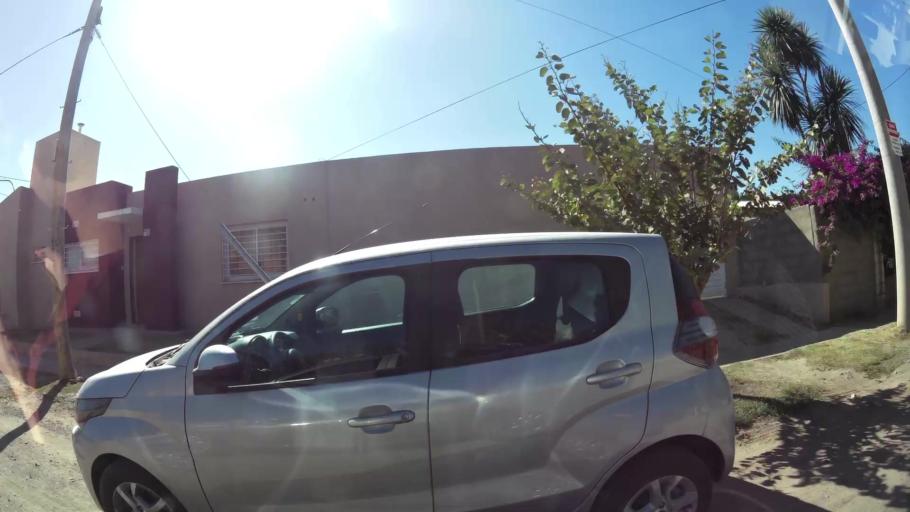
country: AR
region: Cordoba
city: Villa Allende
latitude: -31.3396
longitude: -64.2400
